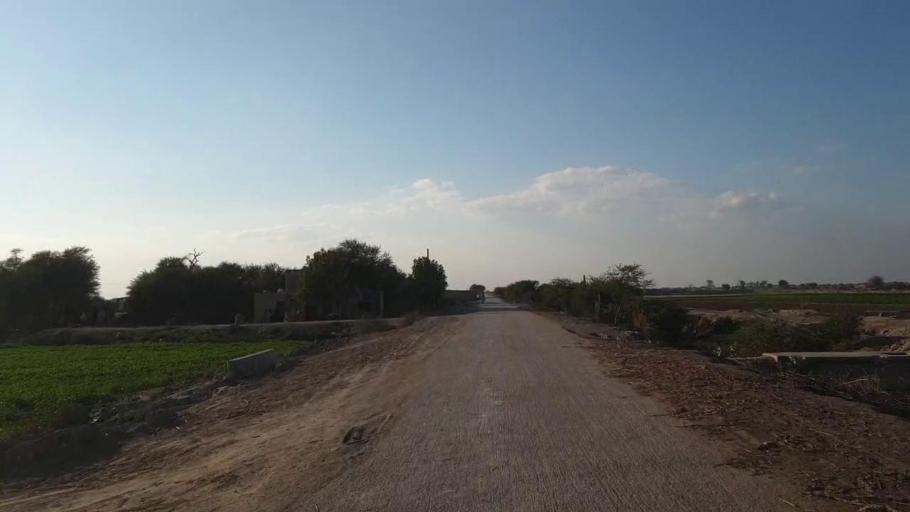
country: PK
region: Sindh
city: Shahpur Chakar
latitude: 26.1440
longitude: 68.5407
